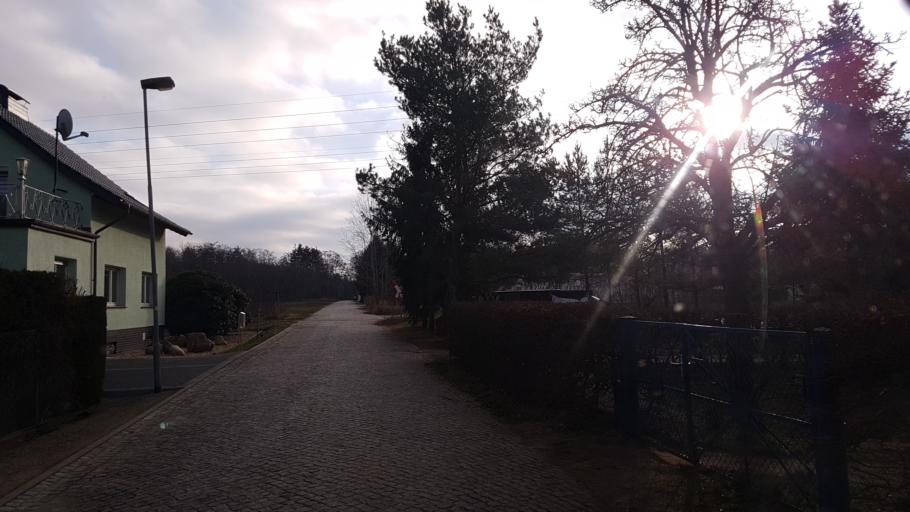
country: DE
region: Brandenburg
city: Sallgast
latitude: 51.5932
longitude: 13.7852
